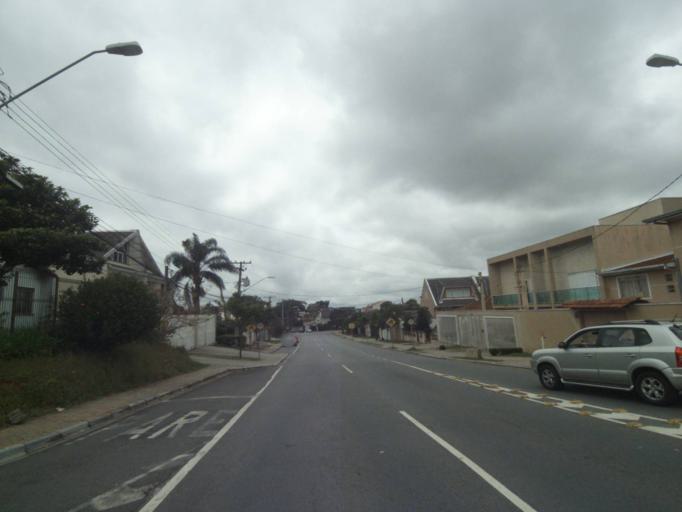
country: BR
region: Parana
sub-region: Pinhais
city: Pinhais
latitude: -25.4376
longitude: -49.2326
